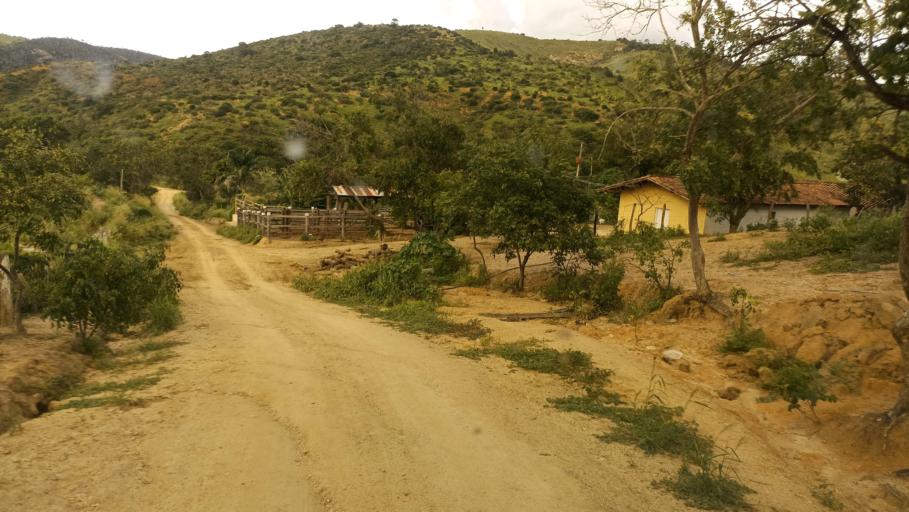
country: BR
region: Minas Gerais
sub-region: Almenara
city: Almenara
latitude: -16.5374
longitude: -40.4418
